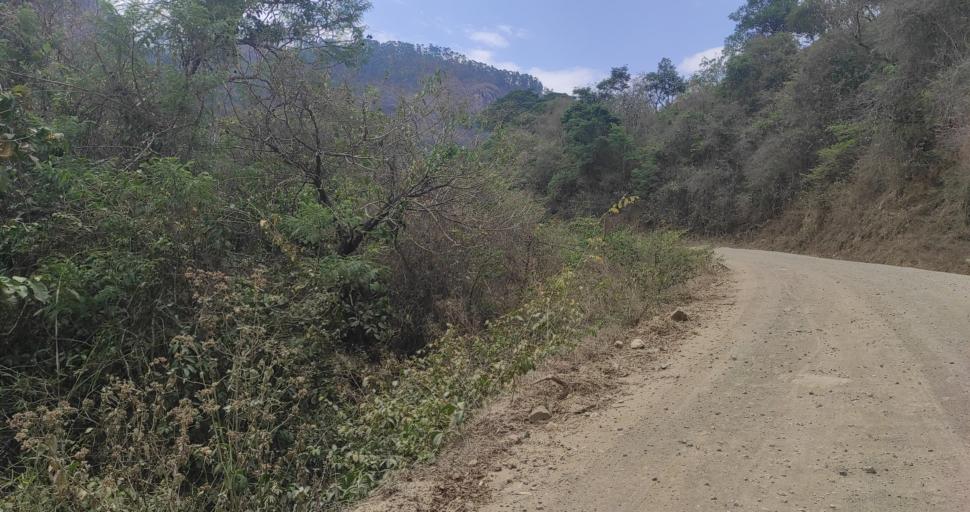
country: EC
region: Loja
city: Catacocha
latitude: -4.0277
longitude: -79.6418
